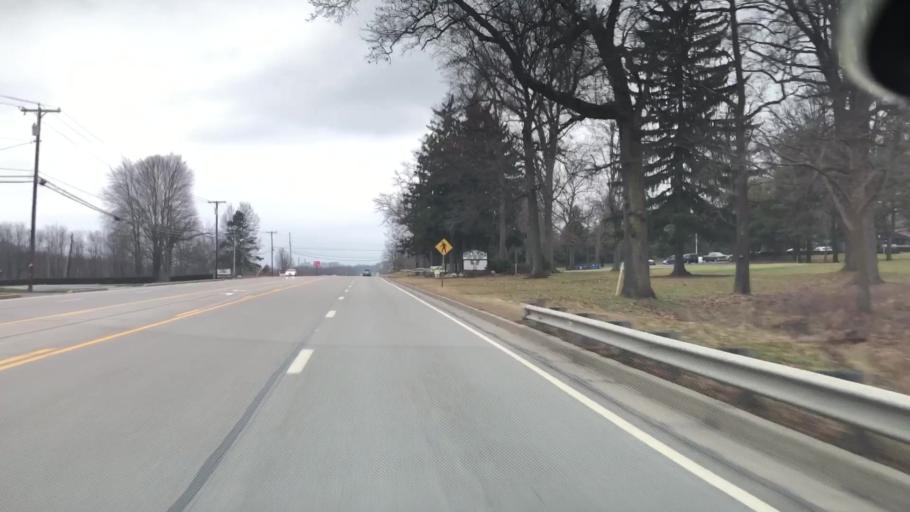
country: US
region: Pennsylvania
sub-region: Mercer County
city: Hermitage
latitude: 41.1925
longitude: -80.4560
